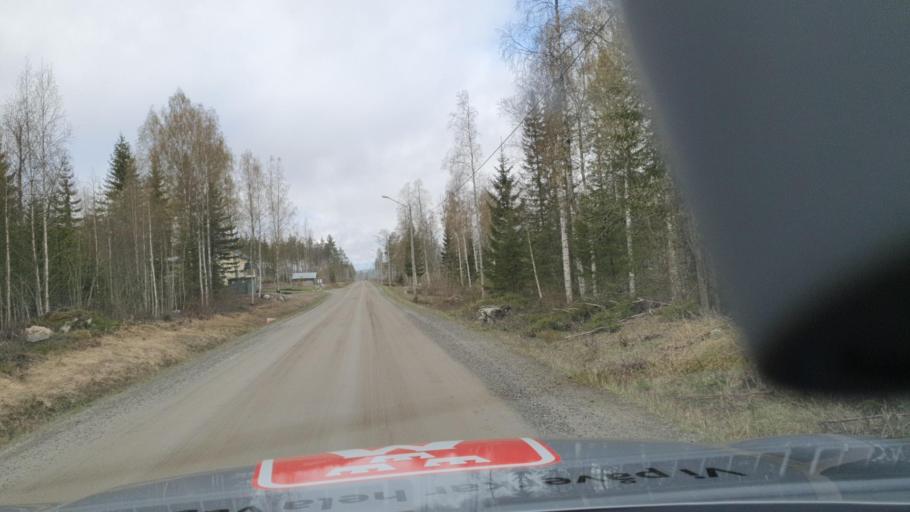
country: SE
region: Vaesterbotten
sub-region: Bjurholms Kommun
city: Bjurholm
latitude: 63.6545
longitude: 19.0390
